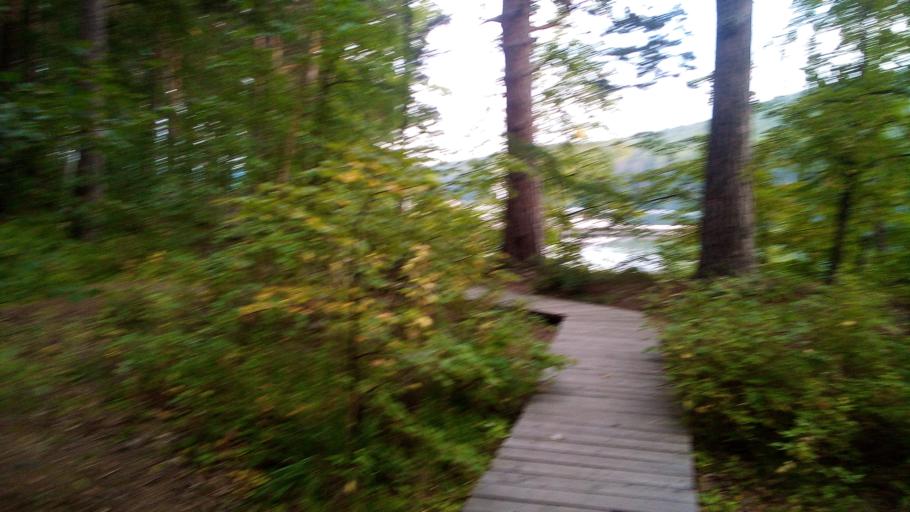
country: RU
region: Chelyabinsk
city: Turgoyak
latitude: 55.1604
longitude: 60.0308
